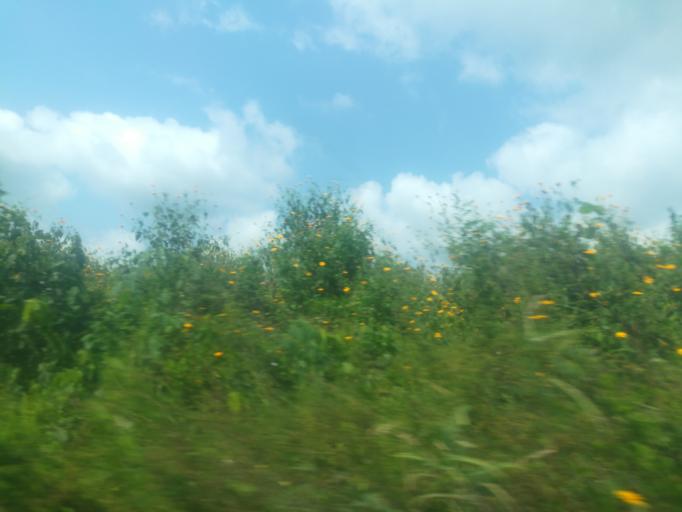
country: NG
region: Oyo
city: Moniya
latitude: 7.5737
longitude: 3.9106
